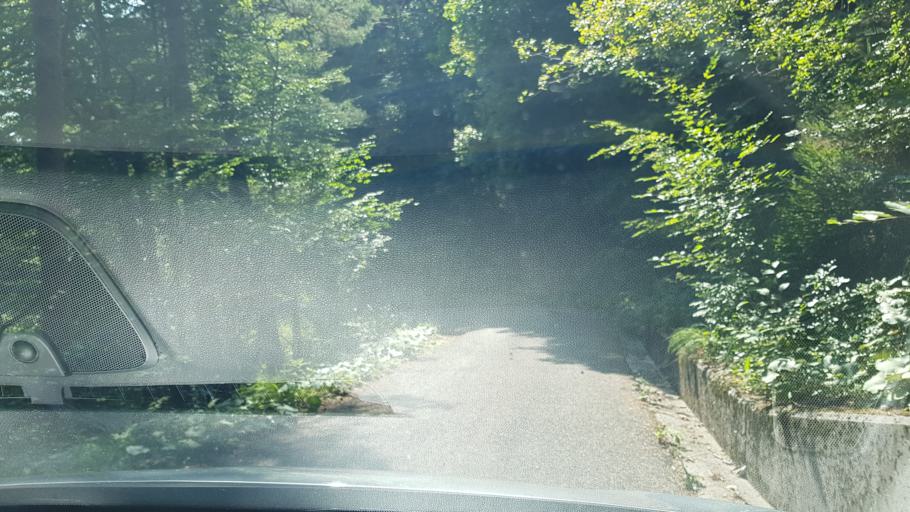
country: IT
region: Friuli Venezia Giulia
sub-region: Provincia di Udine
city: Moggio Udinese
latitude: 46.4441
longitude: 13.2134
